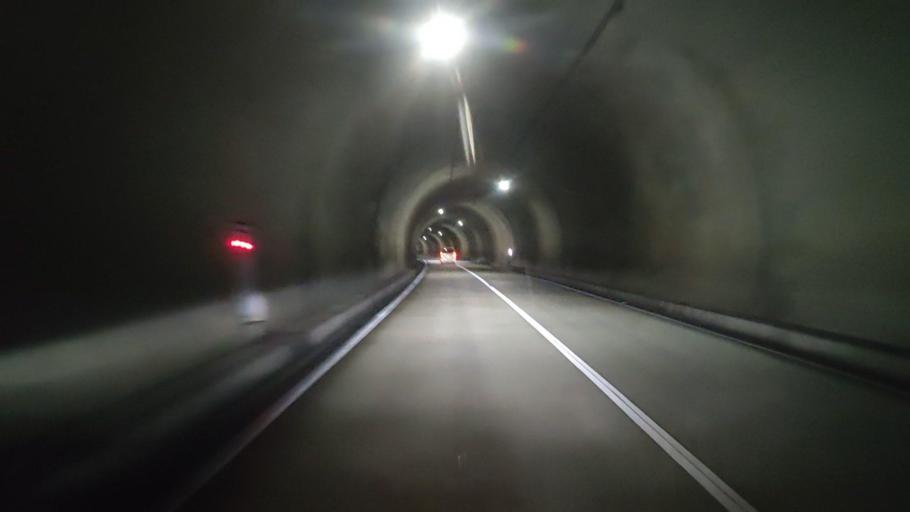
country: JP
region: Wakayama
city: Shingu
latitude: 33.8850
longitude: 135.8789
